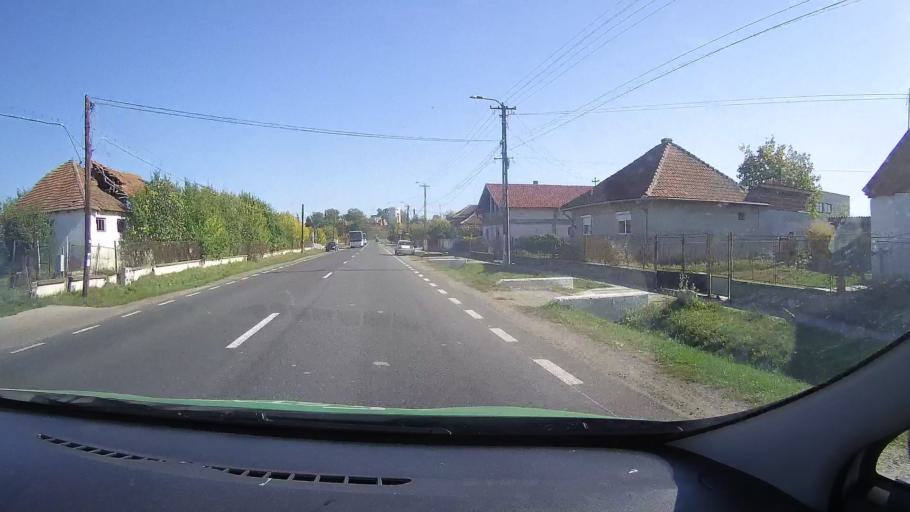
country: RO
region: Satu Mare
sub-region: Oras Ardud
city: Ardud
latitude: 47.6513
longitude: 22.8897
